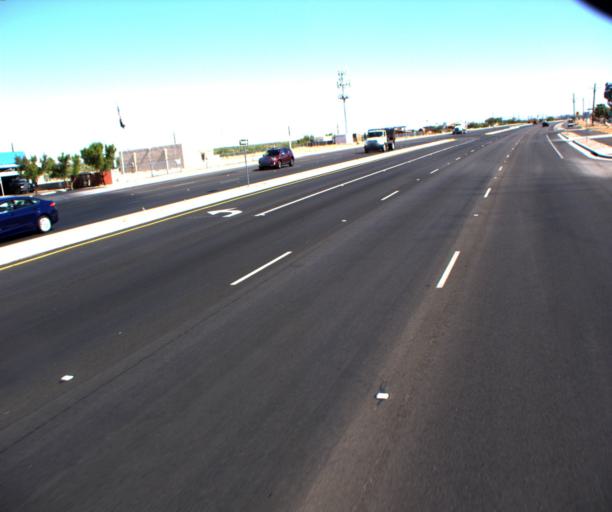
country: US
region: Arizona
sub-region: Pima County
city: Catalina
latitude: 32.4965
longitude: -110.9259
